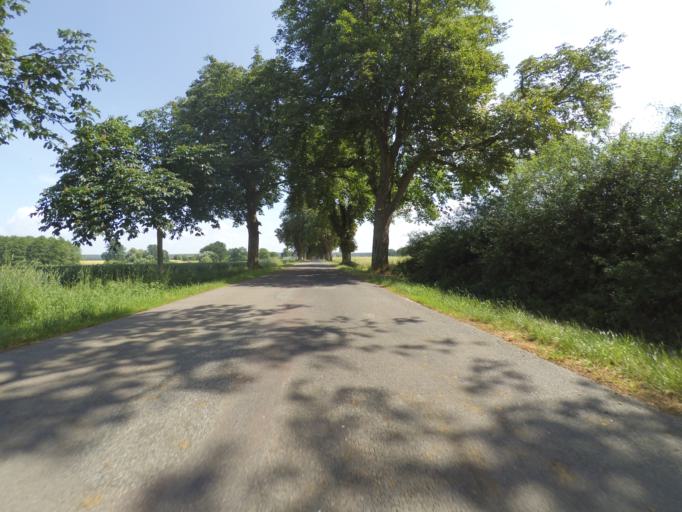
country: DE
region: Mecklenburg-Vorpommern
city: Lubz
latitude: 53.4335
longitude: 12.1337
